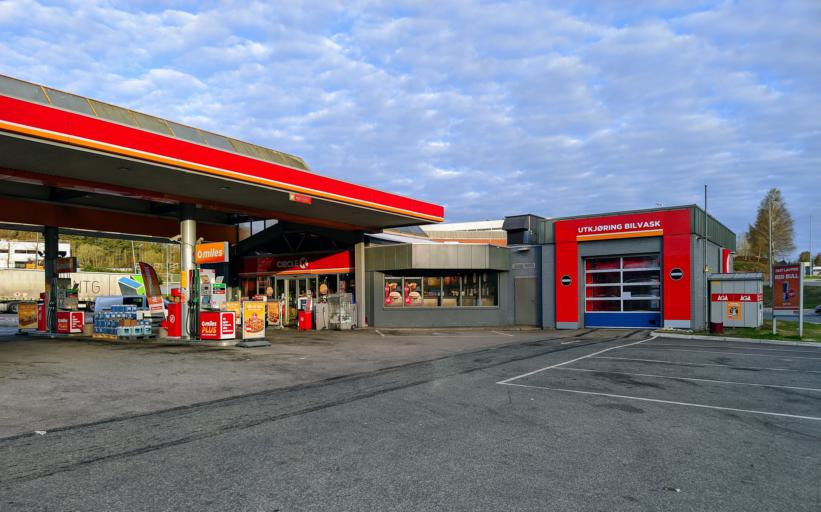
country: NO
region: Telemark
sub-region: Porsgrunn
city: Porsgrunn
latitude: 59.1213
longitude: 9.7093
